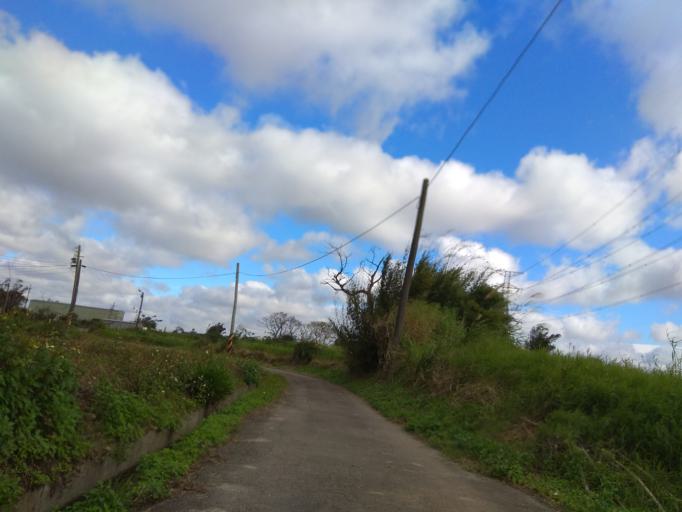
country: TW
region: Taiwan
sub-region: Hsinchu
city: Zhubei
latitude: 24.9702
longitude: 121.0771
